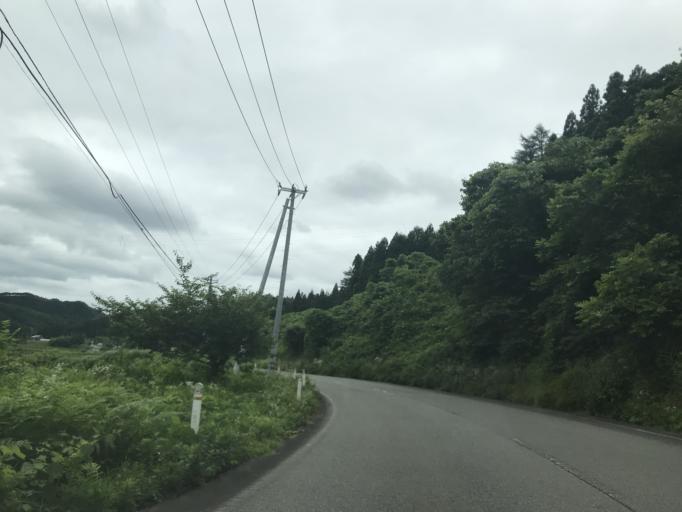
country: JP
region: Iwate
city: Ichinoseki
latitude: 38.9013
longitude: 140.9927
